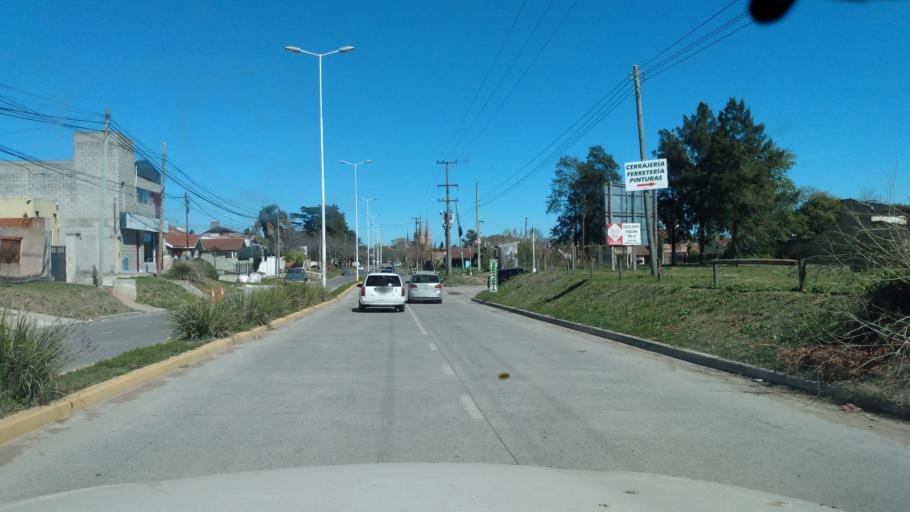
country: AR
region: Buenos Aires
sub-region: Partido de Lujan
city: Lujan
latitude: -34.5582
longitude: -59.1045
